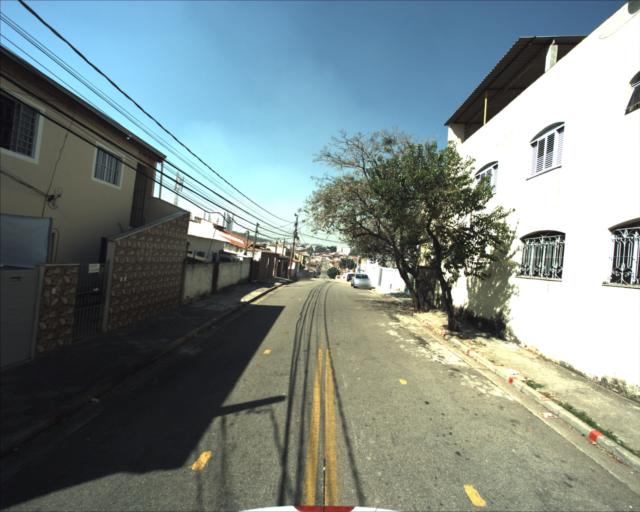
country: BR
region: Sao Paulo
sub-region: Sorocaba
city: Sorocaba
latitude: -23.4998
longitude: -47.4339
